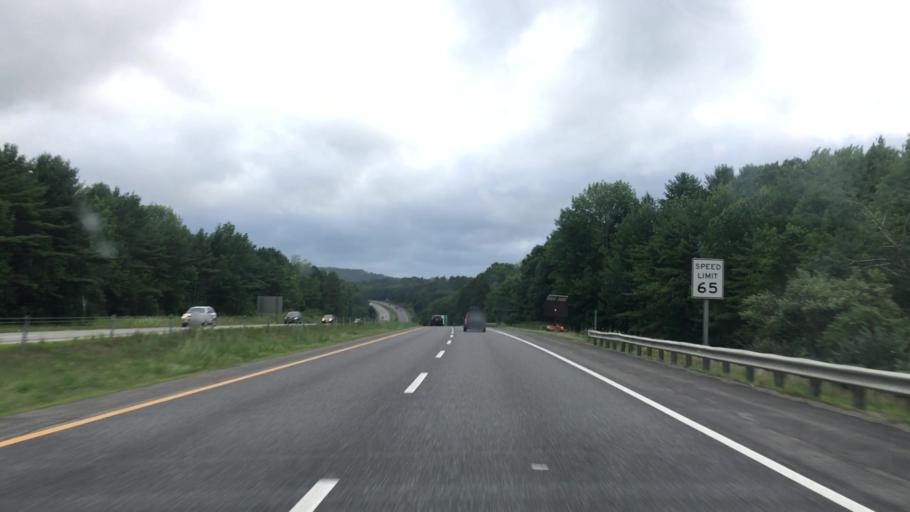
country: US
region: Maine
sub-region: Kennebec County
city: Augusta
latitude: 44.3429
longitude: -69.8007
